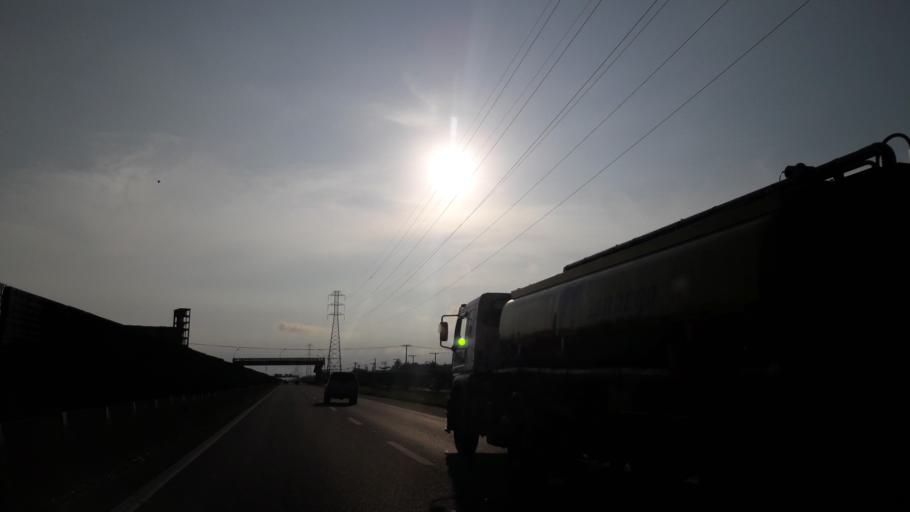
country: BR
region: Sao Paulo
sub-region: Itanhaem
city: Itanhaem
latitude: -24.1461
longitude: -46.7238
